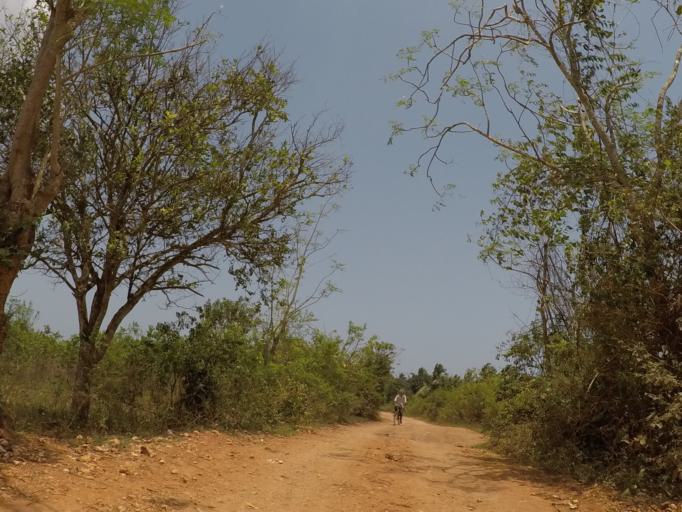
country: TZ
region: Zanzibar Central/South
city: Koani
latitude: -6.1903
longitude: 39.3084
